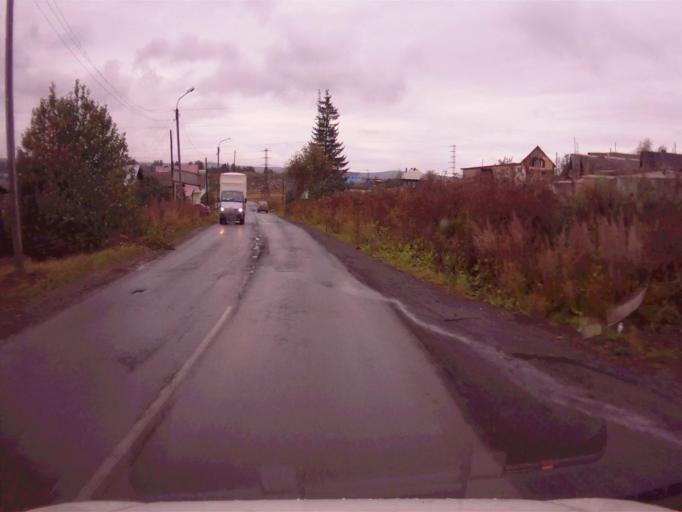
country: RU
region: Chelyabinsk
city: Verkhniy Ufaley
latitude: 56.0599
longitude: 60.2014
